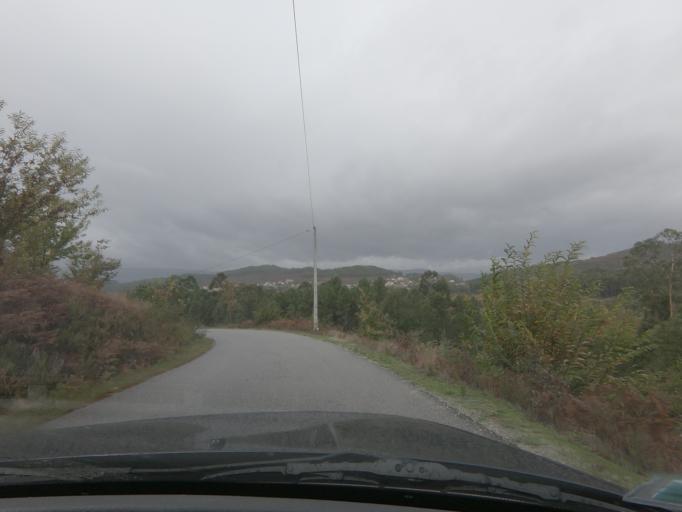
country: PT
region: Vila Real
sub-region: Mondim de Basto
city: Mondim de Basto
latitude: 41.3722
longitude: -7.9419
